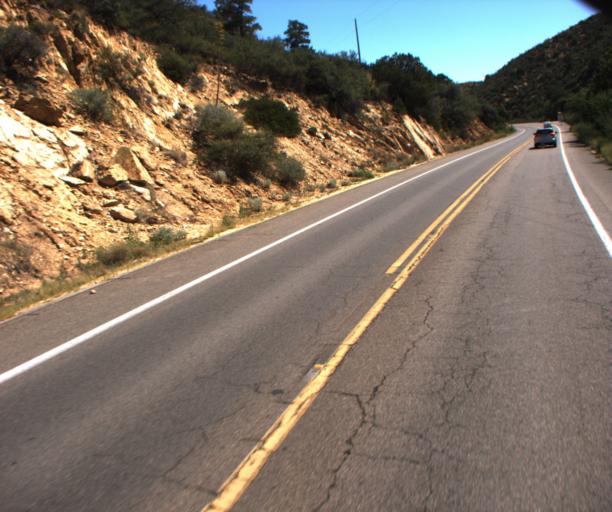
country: US
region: Arizona
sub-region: Gila County
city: Miami
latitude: 33.3774
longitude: -110.9104
